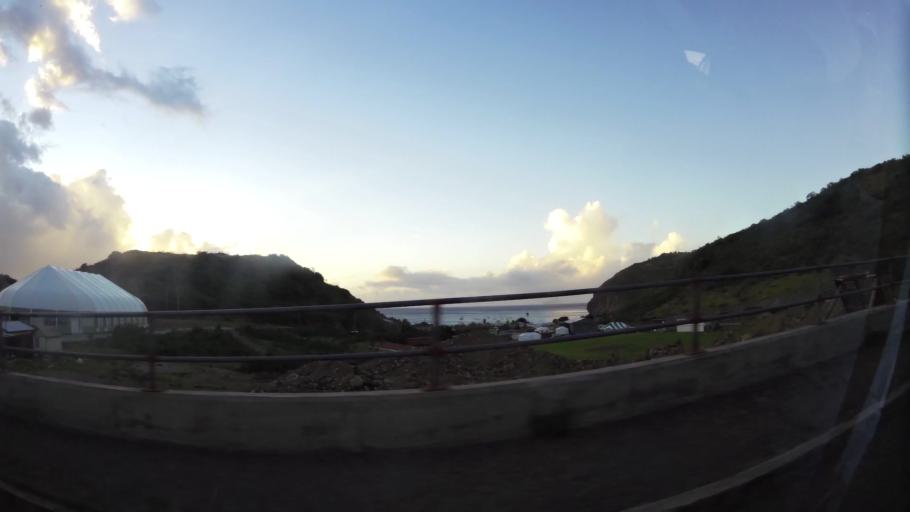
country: MS
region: Saint Peter
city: Brades
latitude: 16.7988
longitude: -62.2021
